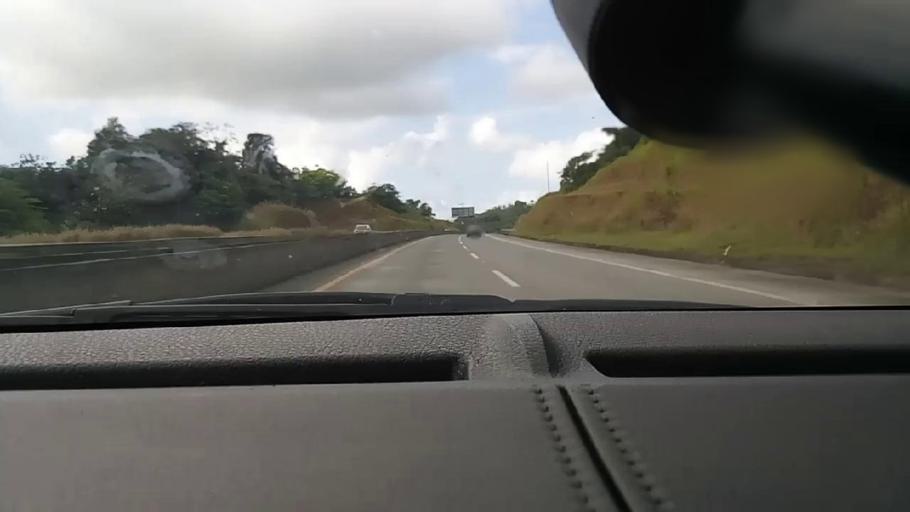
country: PA
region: Colon
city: Gatun
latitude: 9.2809
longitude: -79.7545
